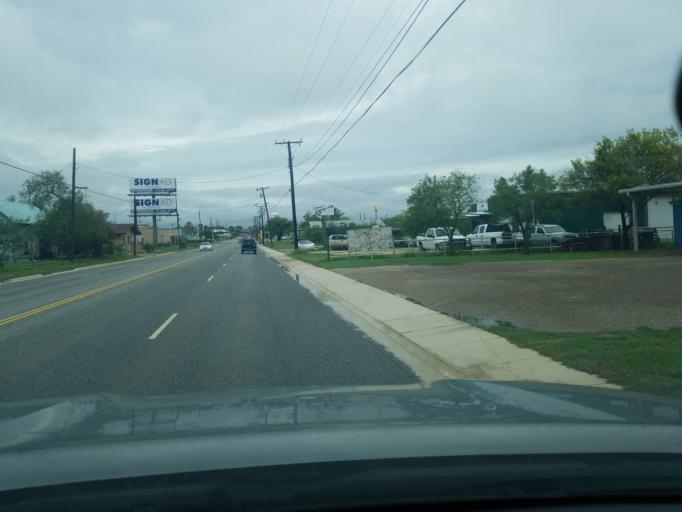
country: US
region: Texas
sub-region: Dimmit County
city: Carrizo Springs
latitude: 28.5220
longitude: -99.8537
